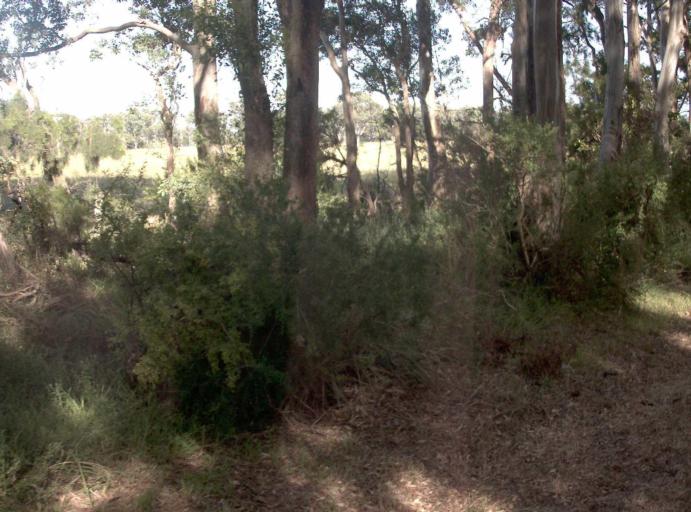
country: AU
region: Victoria
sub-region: East Gippsland
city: Lakes Entrance
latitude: -37.8052
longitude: 147.8398
